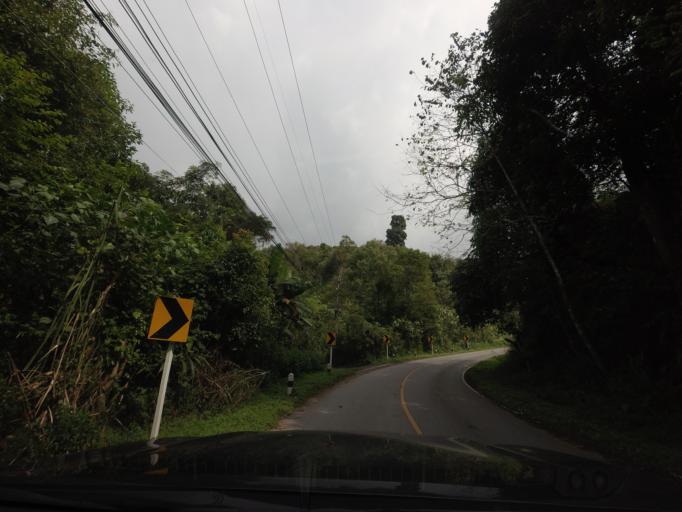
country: TH
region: Nan
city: Bo Kluea
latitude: 19.2066
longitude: 101.0738
